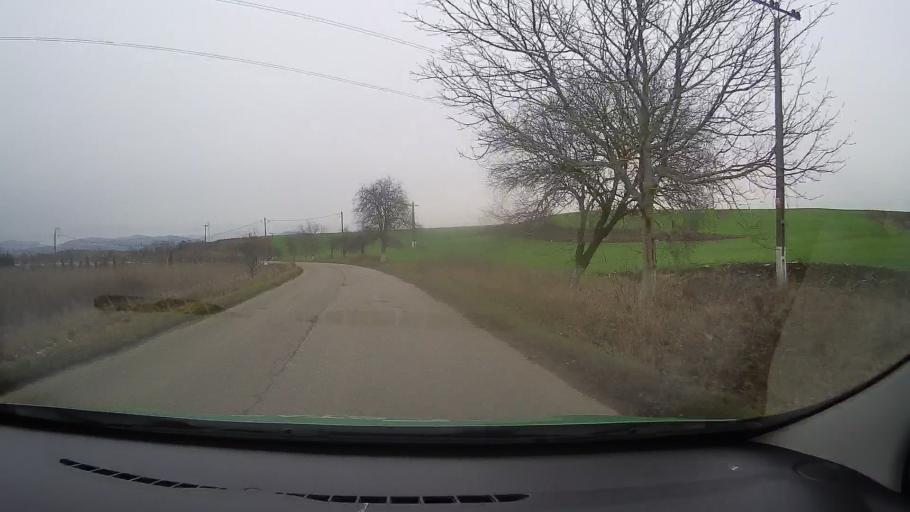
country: RO
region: Hunedoara
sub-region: Comuna Romos
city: Romos
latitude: 45.8718
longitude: 23.2684
